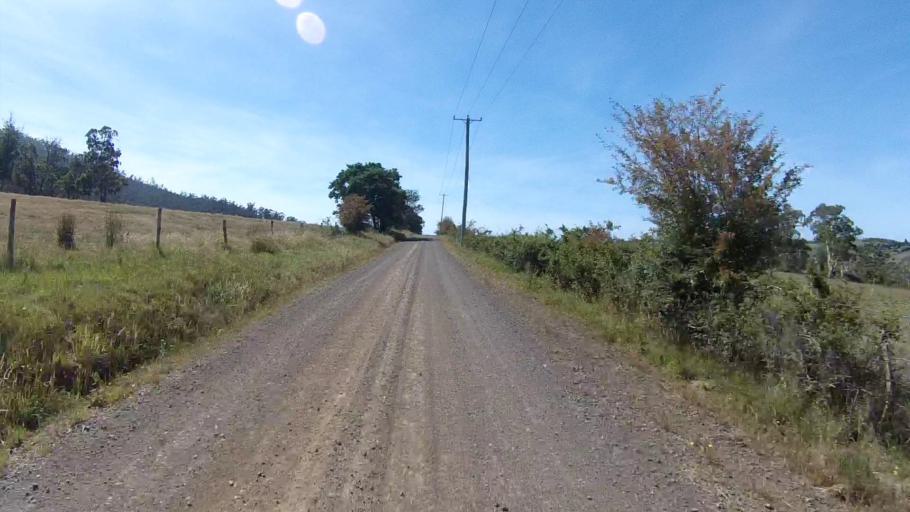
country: AU
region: Tasmania
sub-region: Sorell
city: Sorell
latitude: -42.7481
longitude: 147.6195
